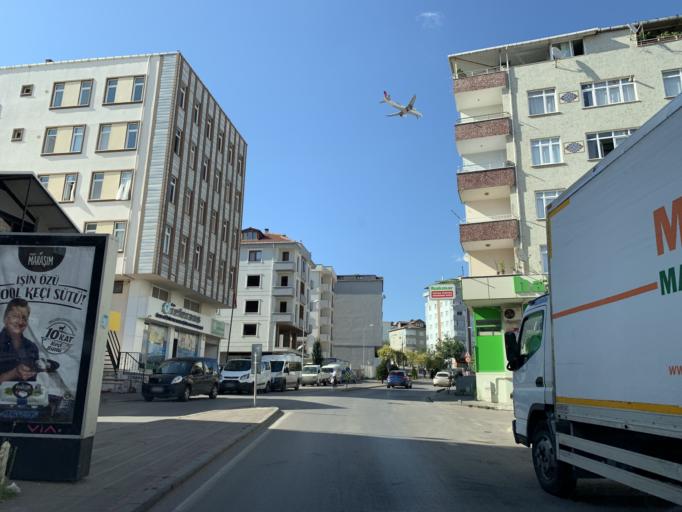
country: TR
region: Istanbul
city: Pendik
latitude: 40.8801
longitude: 29.2670
